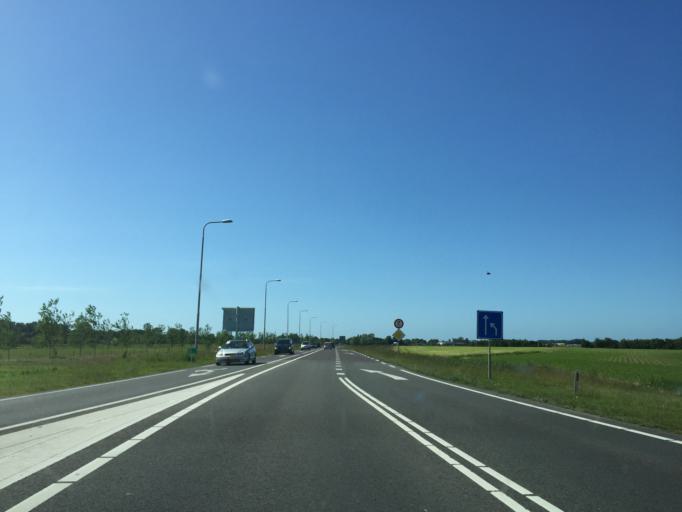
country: NL
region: Zeeland
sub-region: Gemeente Middelburg
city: Middelburg
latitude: 51.5200
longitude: 3.6198
